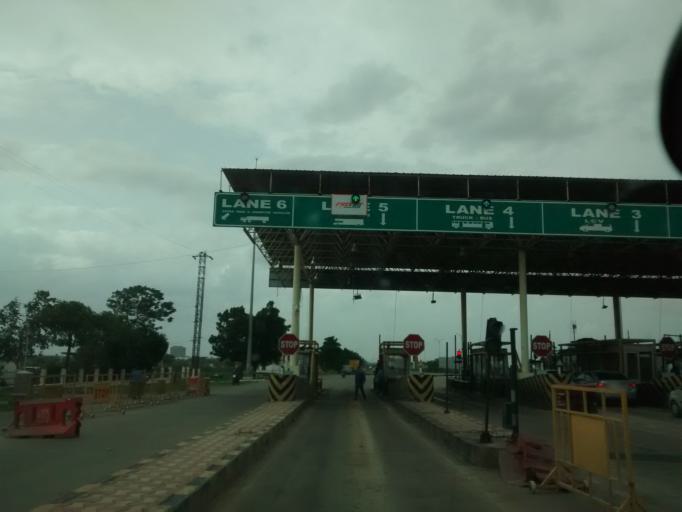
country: IN
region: Telangana
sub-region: Mahbubnagar
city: Alampur
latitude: 15.8874
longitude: 78.0168
